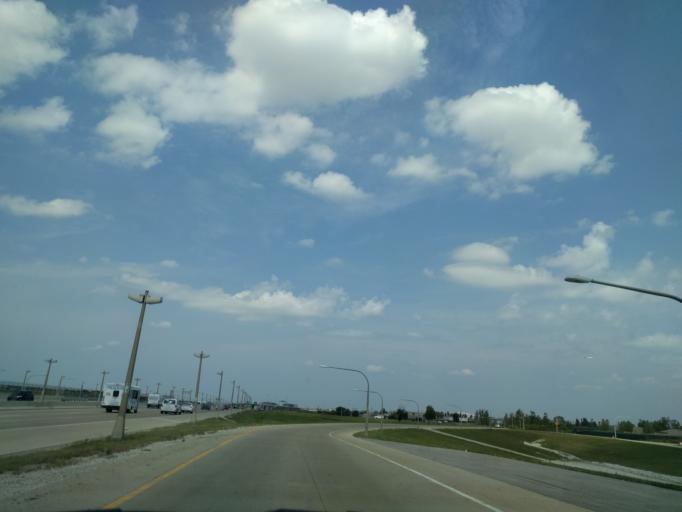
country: US
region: Illinois
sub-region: Cook County
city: Schiller Park
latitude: 41.9696
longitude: -87.8764
